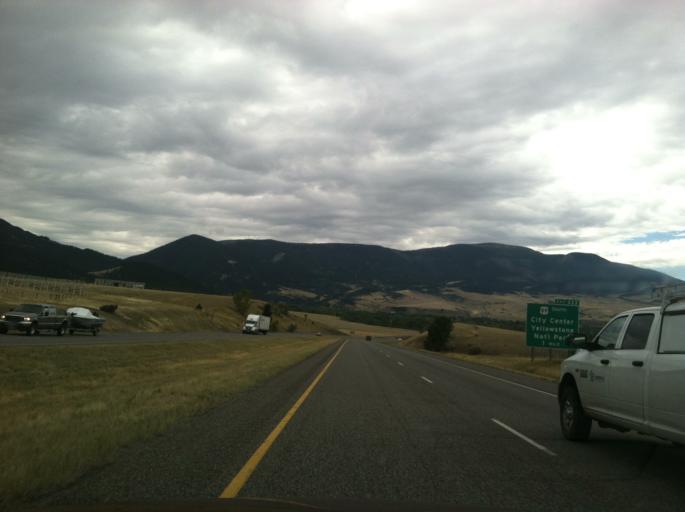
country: US
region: Montana
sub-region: Park County
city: Livingston
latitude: 45.6473
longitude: -110.5491
